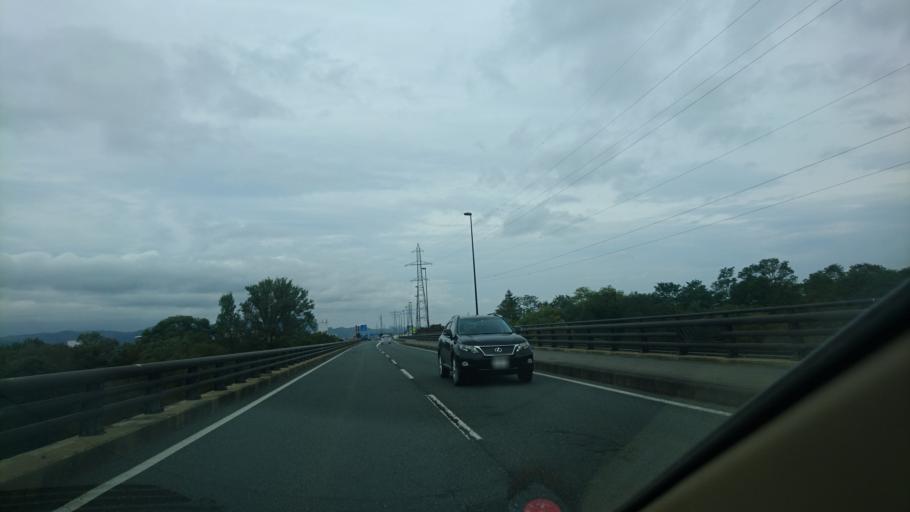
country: JP
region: Iwate
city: Morioka-shi
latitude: 39.7057
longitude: 141.1018
